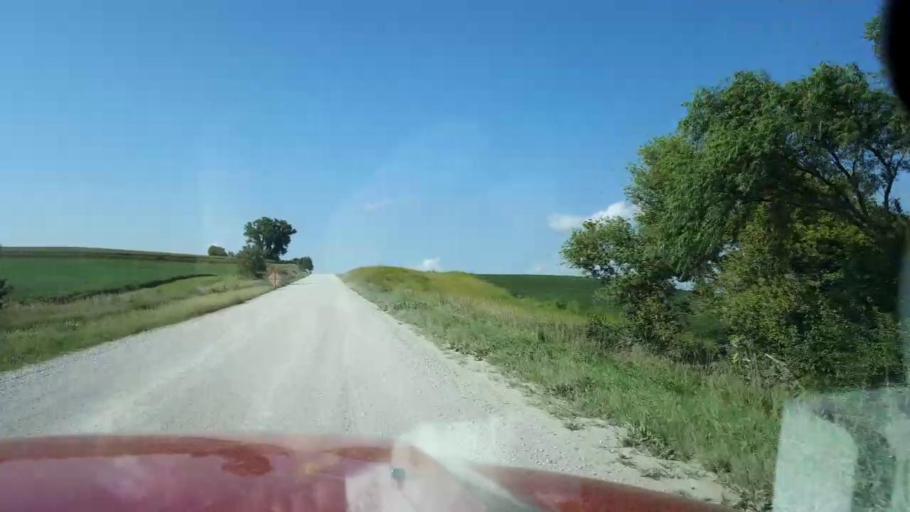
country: US
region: Iowa
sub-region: Pottawattamie County
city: Oakland
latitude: 41.2539
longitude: -95.5370
